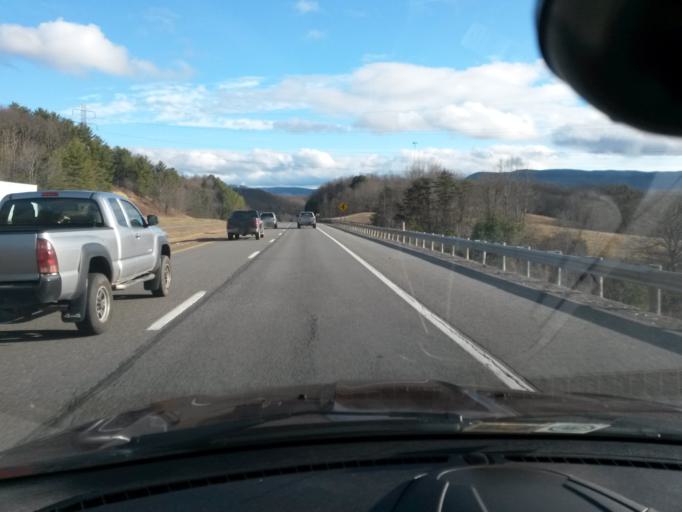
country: US
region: West Virginia
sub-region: Mercer County
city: Athens
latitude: 37.3565
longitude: -81.0229
